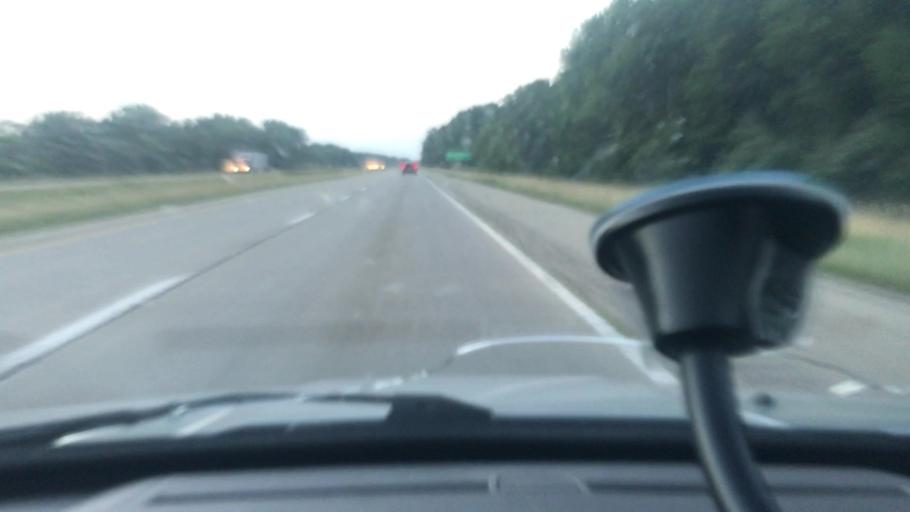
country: US
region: Illinois
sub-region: Peoria County
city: Bellevue
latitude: 40.7633
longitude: -89.6704
